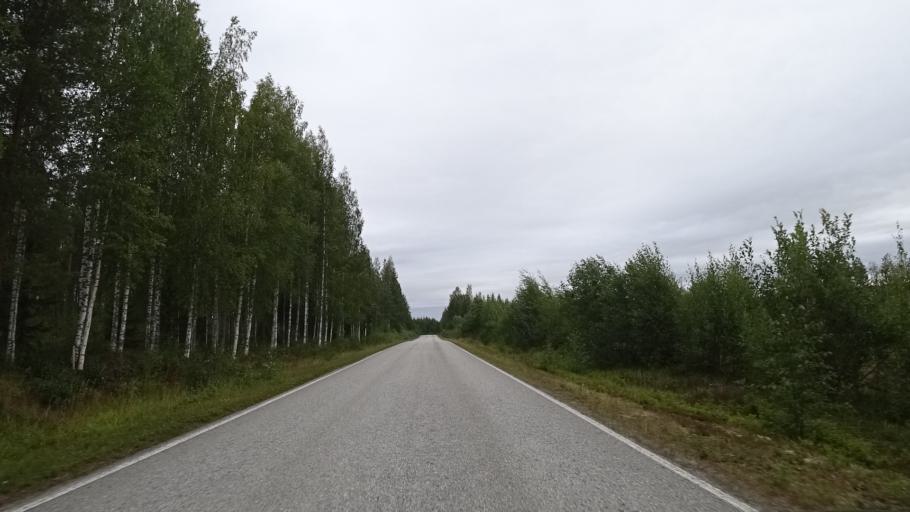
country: FI
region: North Karelia
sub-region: Pielisen Karjala
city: Lieksa
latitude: 63.3539
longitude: 30.2636
